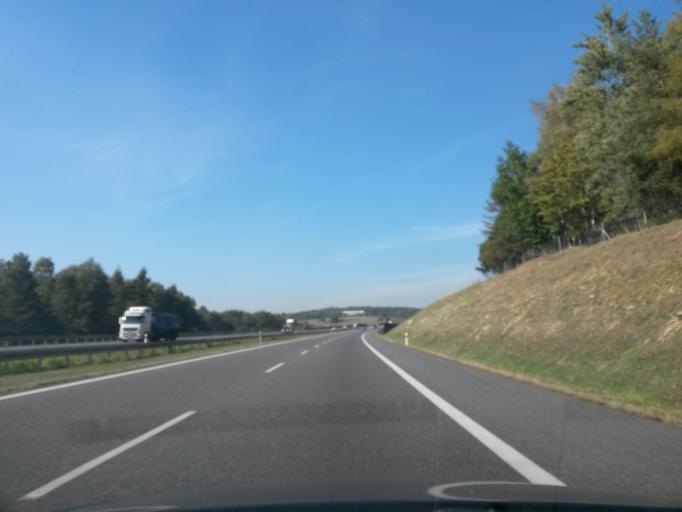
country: PL
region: Lesser Poland Voivodeship
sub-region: Powiat oswiecimski
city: Chelmek
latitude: 50.1537
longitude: 19.2390
